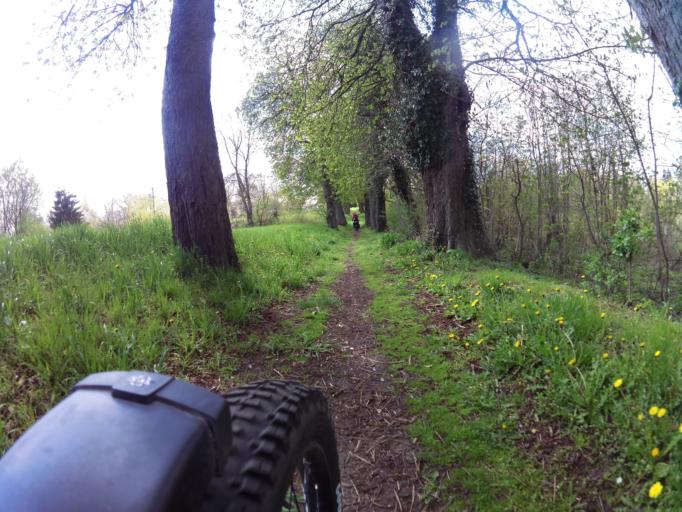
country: PL
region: West Pomeranian Voivodeship
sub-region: Powiat gryficki
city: Gryfice
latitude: 53.8624
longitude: 15.1635
